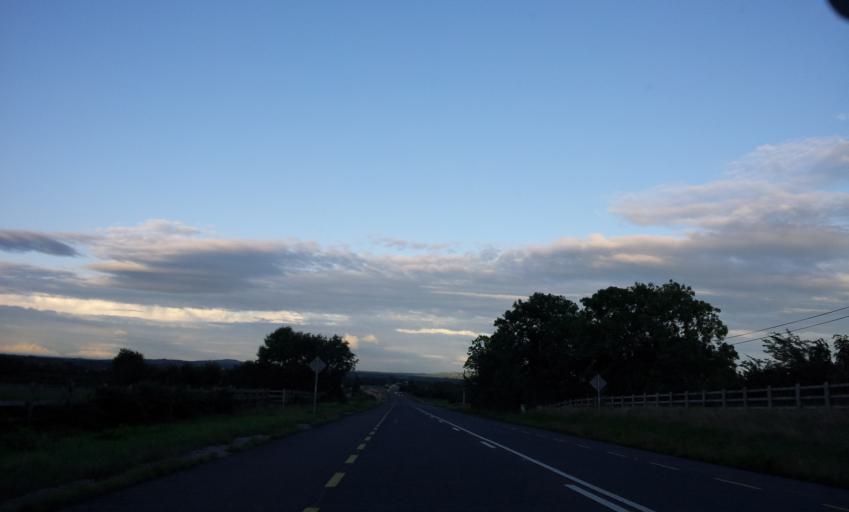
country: IE
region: Munster
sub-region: County Limerick
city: Newcastle West
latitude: 52.4355
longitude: -9.1109
